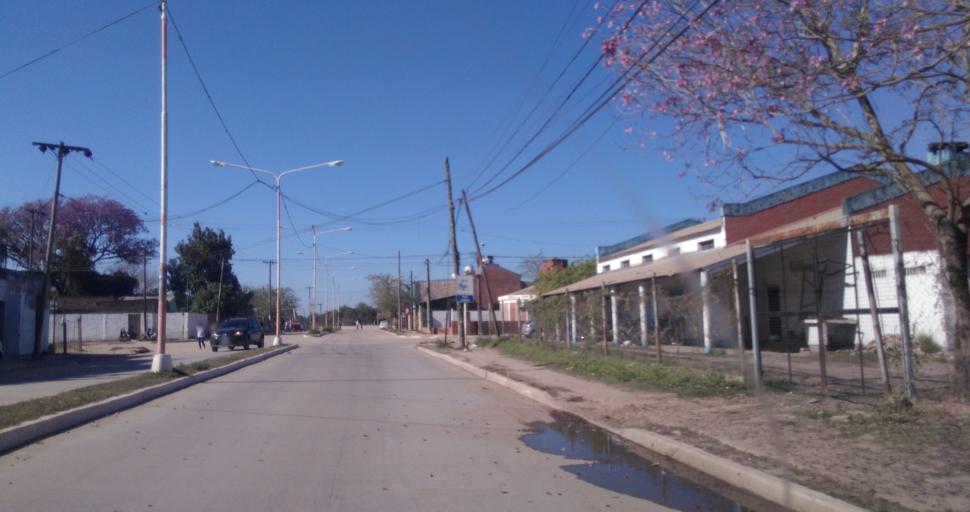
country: AR
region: Chaco
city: Resistencia
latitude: -27.4515
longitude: -58.9657
